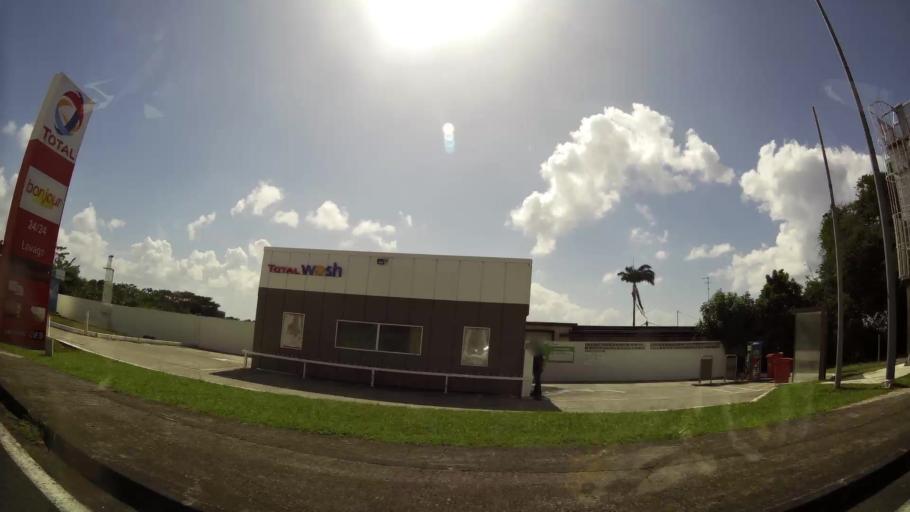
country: MQ
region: Martinique
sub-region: Martinique
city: Fort-de-France
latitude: 14.6088
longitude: -61.0956
